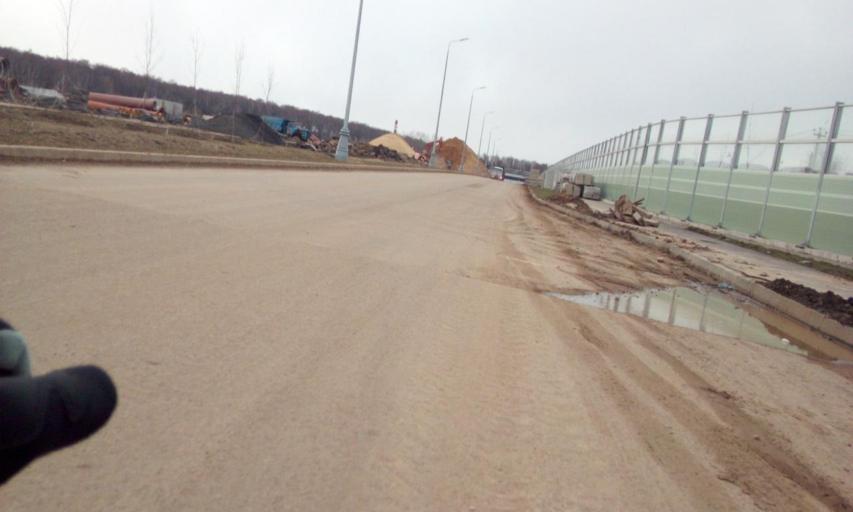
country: RU
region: Moskovskaya
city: Kommunarka
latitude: 55.5234
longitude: 37.4780
